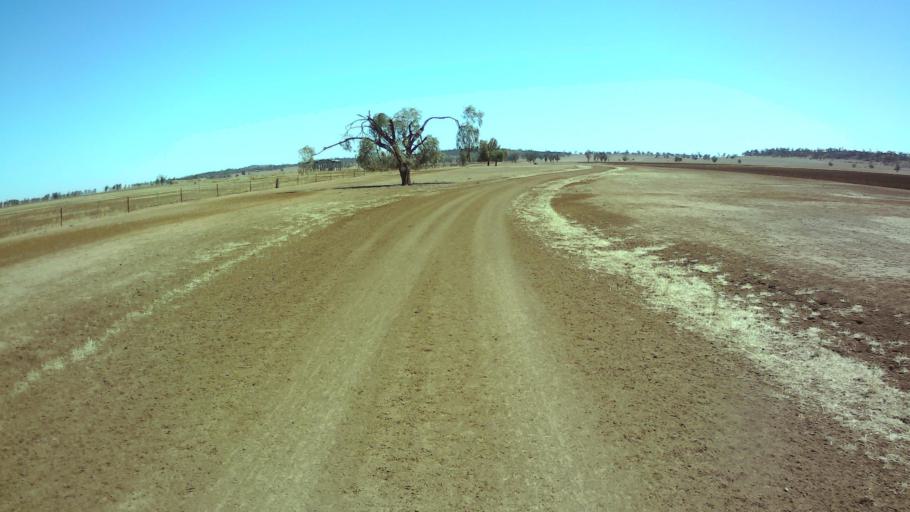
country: AU
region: New South Wales
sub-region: Forbes
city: Forbes
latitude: -33.7082
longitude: 147.6680
